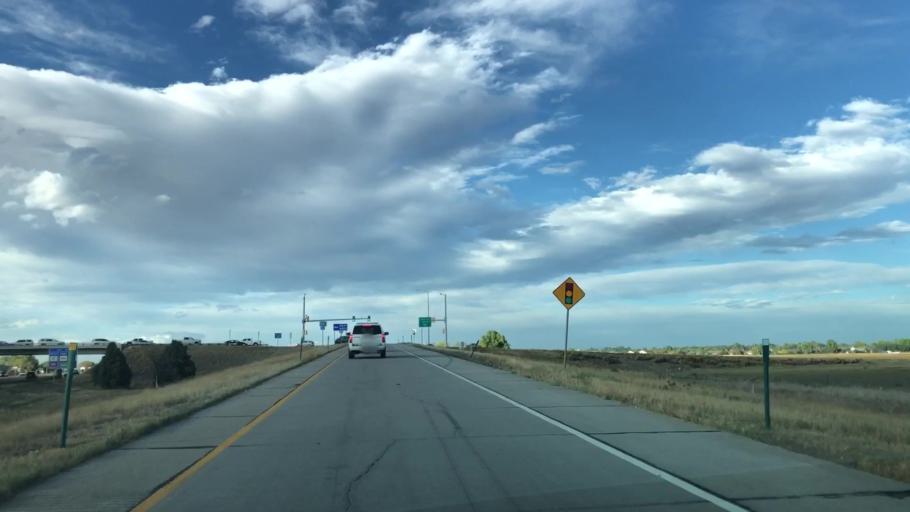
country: US
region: Colorado
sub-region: Larimer County
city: Fort Collins
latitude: 40.5649
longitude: -105.0009
